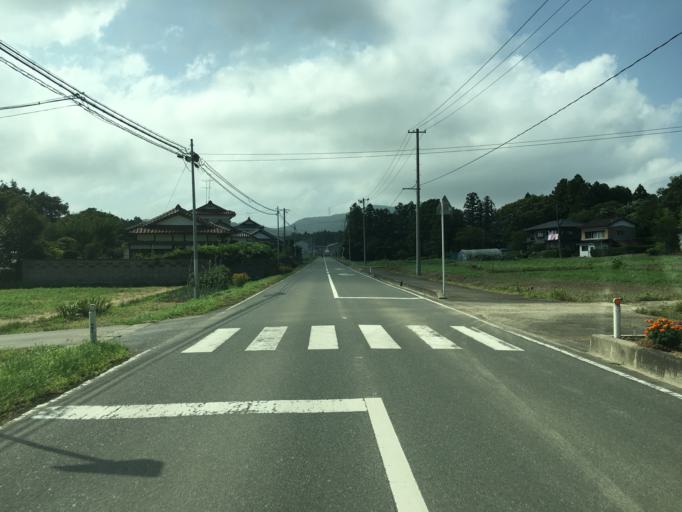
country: JP
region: Miyagi
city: Marumori
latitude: 37.8403
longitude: 140.8967
